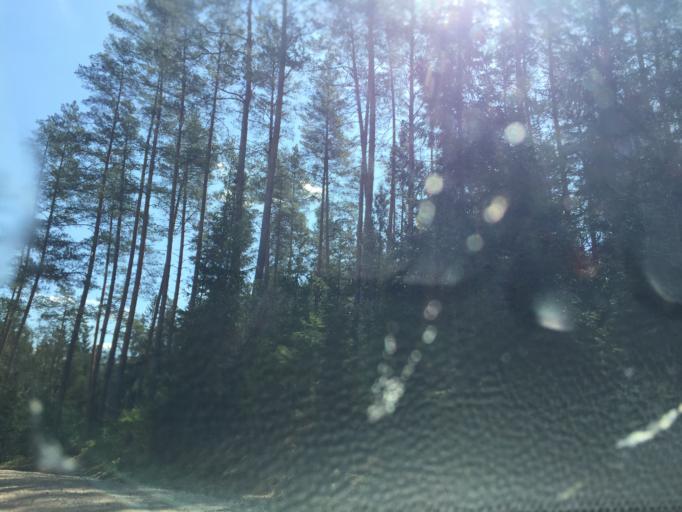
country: LV
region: Vecumnieki
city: Vecumnieki
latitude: 56.6521
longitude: 24.4658
